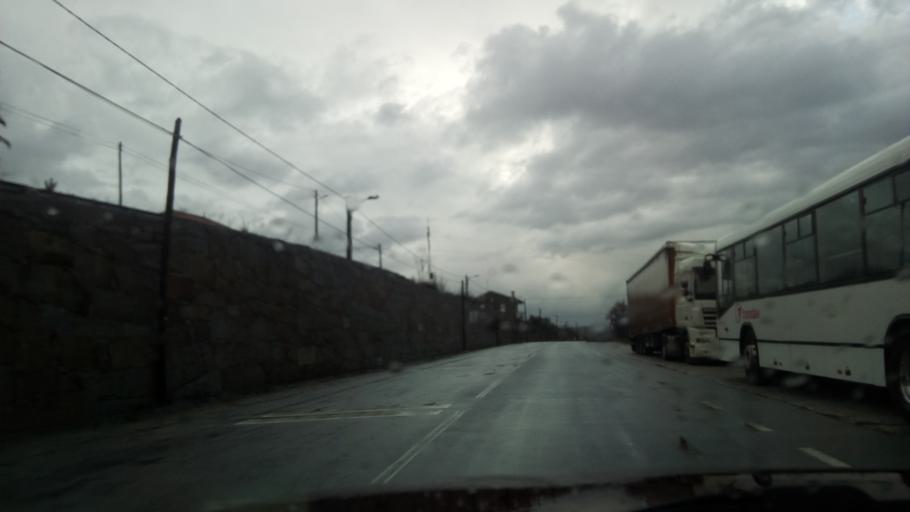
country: PT
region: Guarda
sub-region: Guarda
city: Guarda
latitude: 40.6069
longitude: -7.3016
